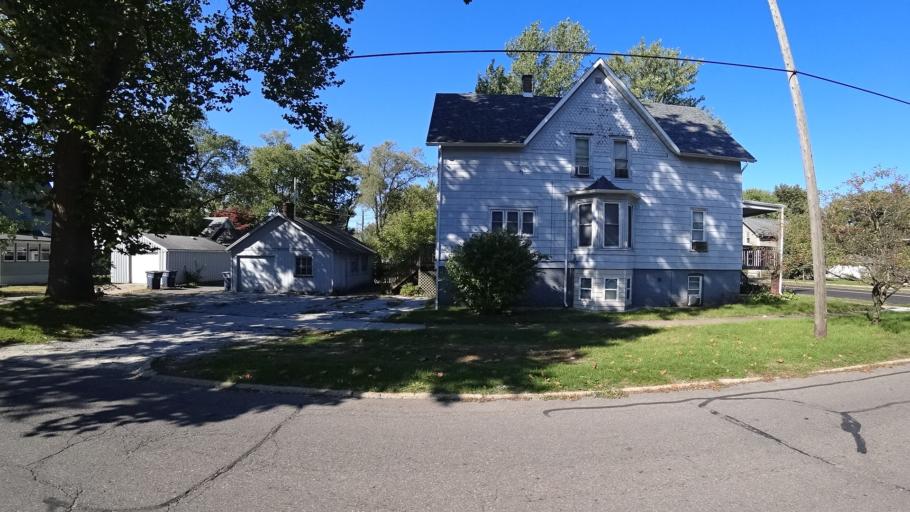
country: US
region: Indiana
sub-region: LaPorte County
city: Michigan City
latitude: 41.7058
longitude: -86.8936
